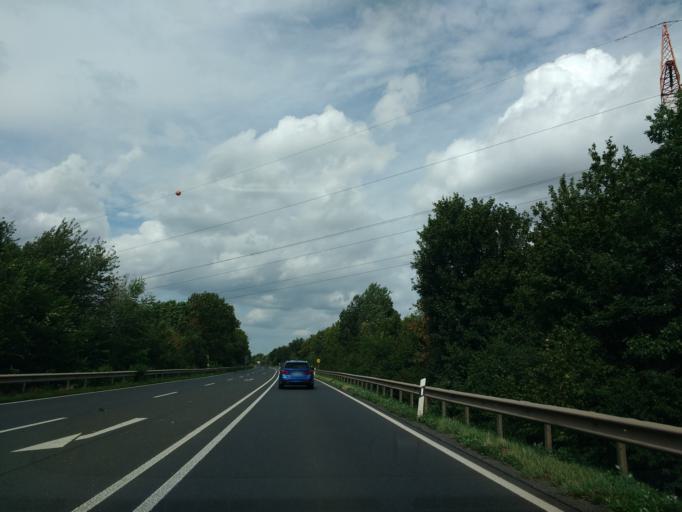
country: DE
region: North Rhine-Westphalia
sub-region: Regierungsbezirk Detmold
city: Petershagen
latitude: 52.3159
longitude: 8.9826
